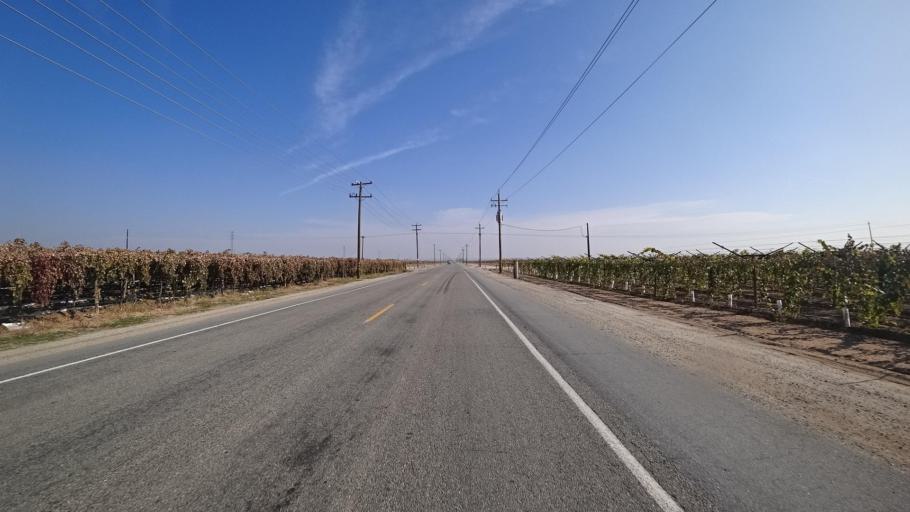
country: US
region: California
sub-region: Kern County
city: Rosedale
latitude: 35.4995
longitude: -119.1357
